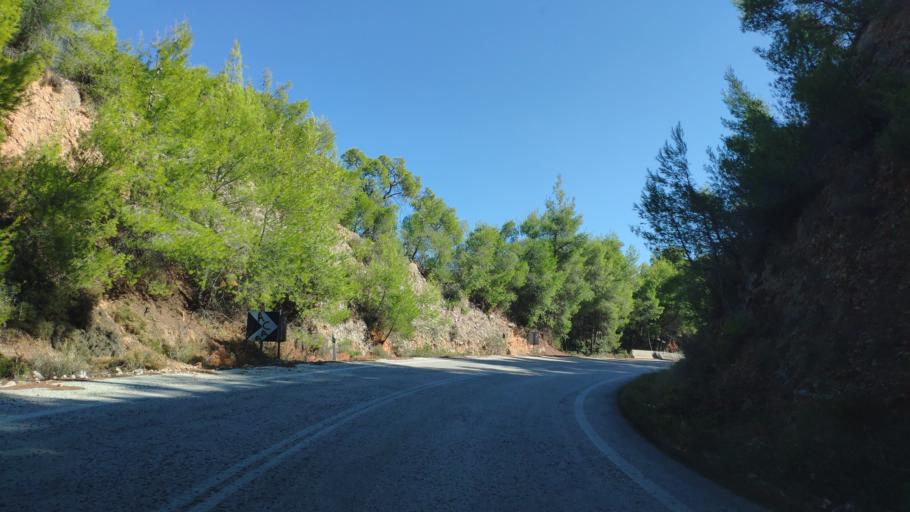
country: GR
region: Peloponnese
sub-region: Nomos Korinthias
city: Sofikon
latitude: 37.8294
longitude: 23.0302
